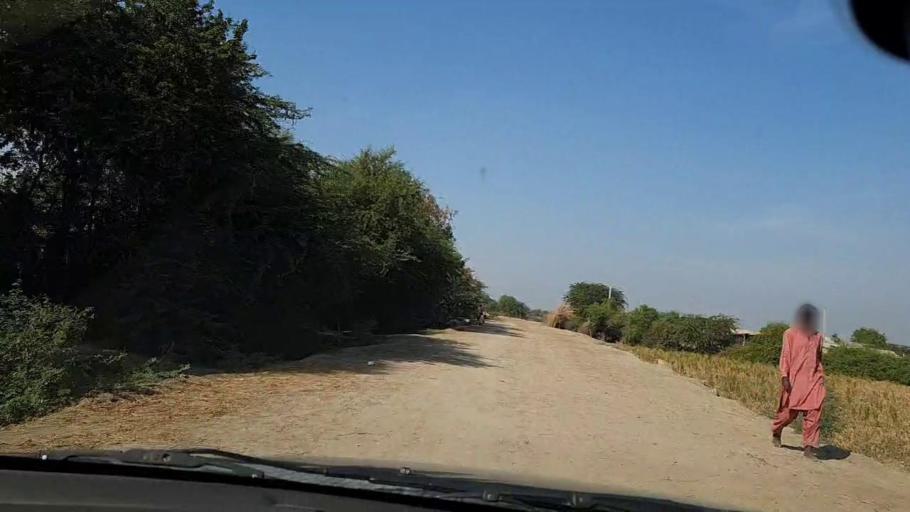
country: PK
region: Sindh
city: Mirpur Batoro
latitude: 24.6522
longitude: 68.2544
